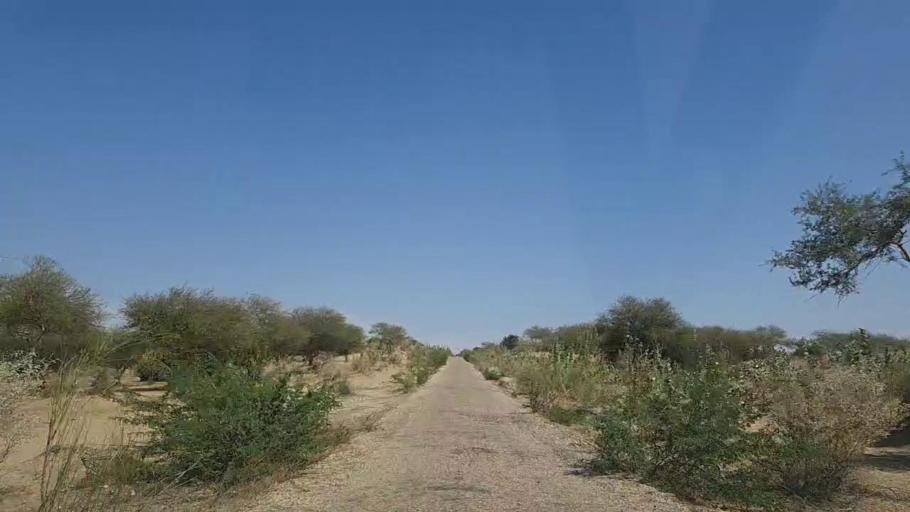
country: PK
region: Sindh
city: Mithi
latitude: 24.8230
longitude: 69.7009
